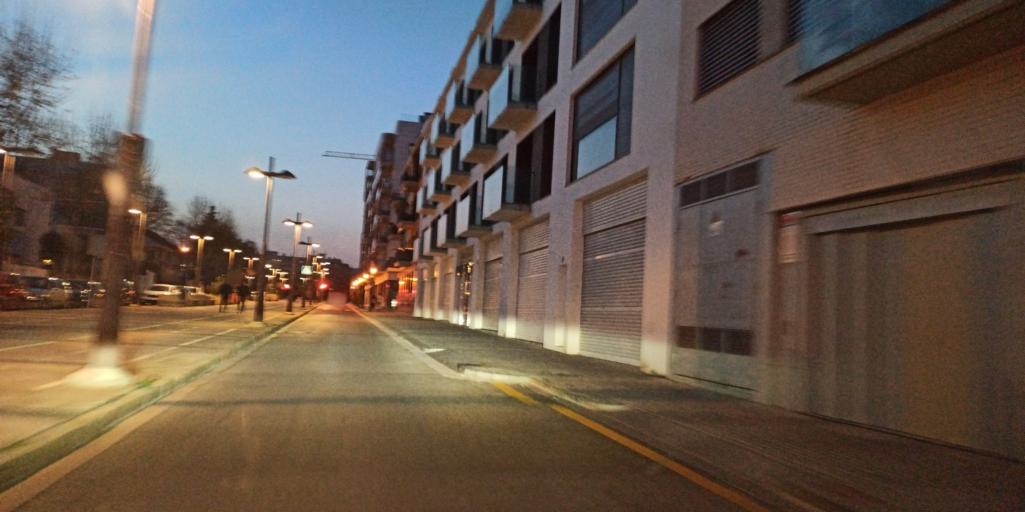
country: ES
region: Catalonia
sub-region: Provincia de Barcelona
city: Vilanova i la Geltru
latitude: 41.2150
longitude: 1.7254
